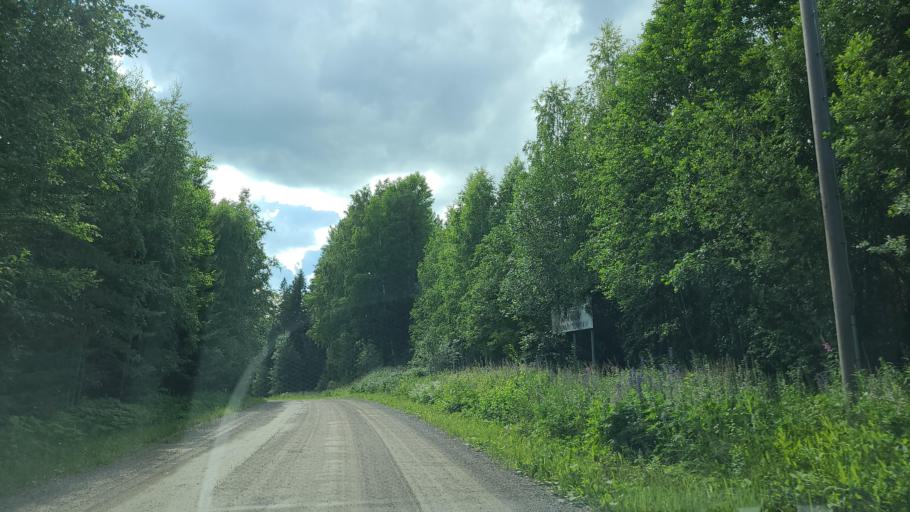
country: FI
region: Central Finland
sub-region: Jaemsae
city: Jaemsae
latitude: 61.9090
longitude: 25.2903
